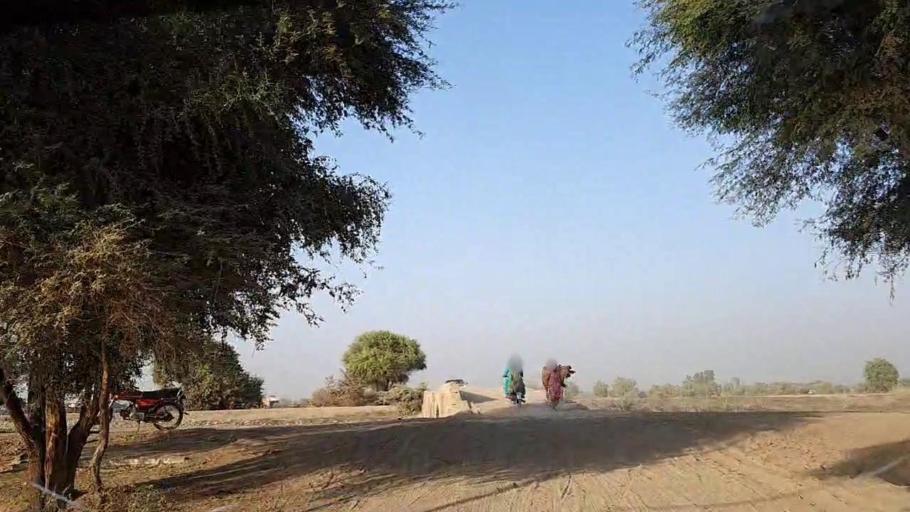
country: PK
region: Sindh
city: Rustam jo Goth
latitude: 27.9736
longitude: 68.8052
